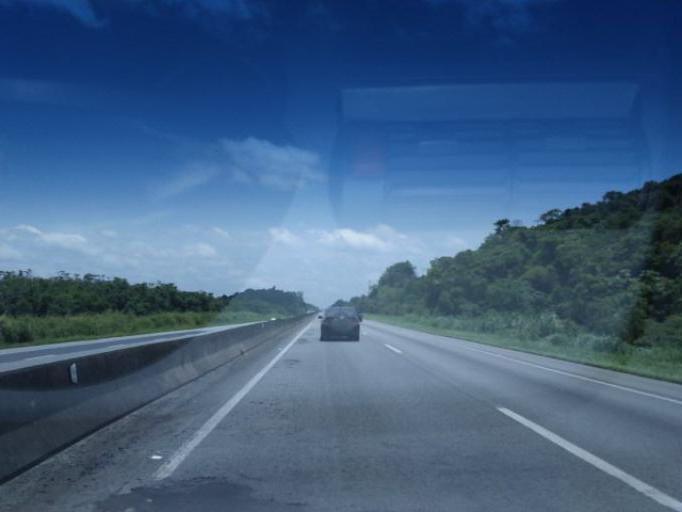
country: BR
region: Sao Paulo
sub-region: Registro
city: Registro
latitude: -24.4339
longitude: -47.7903
